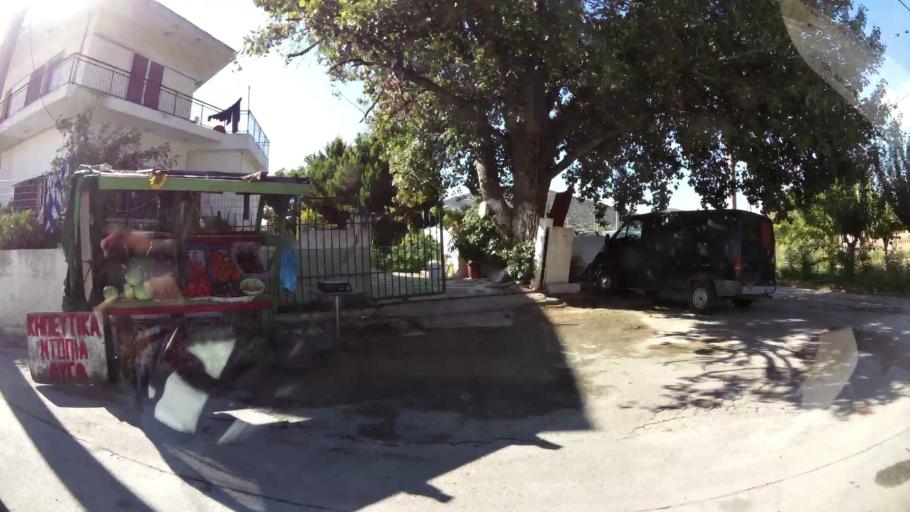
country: GR
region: Attica
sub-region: Nomarchia Anatolikis Attikis
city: Markopoulo
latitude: 37.8812
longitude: 23.9286
